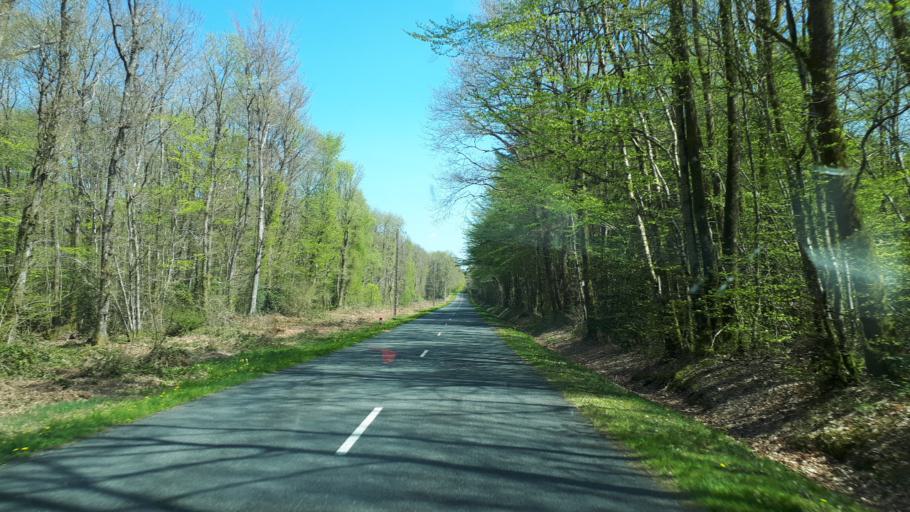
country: FR
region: Centre
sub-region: Departement du Cher
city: Henrichemont
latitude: 47.2914
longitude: 2.6001
